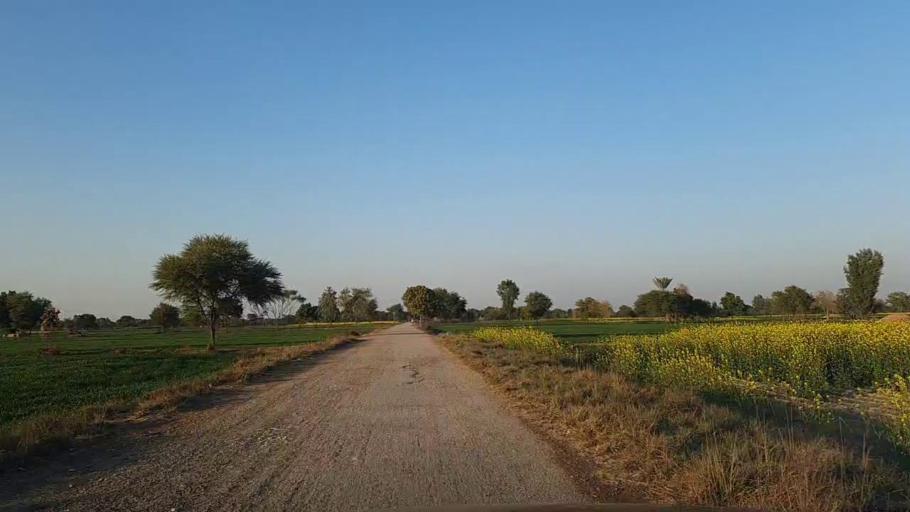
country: PK
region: Sindh
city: Nawabshah
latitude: 26.2351
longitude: 68.3382
